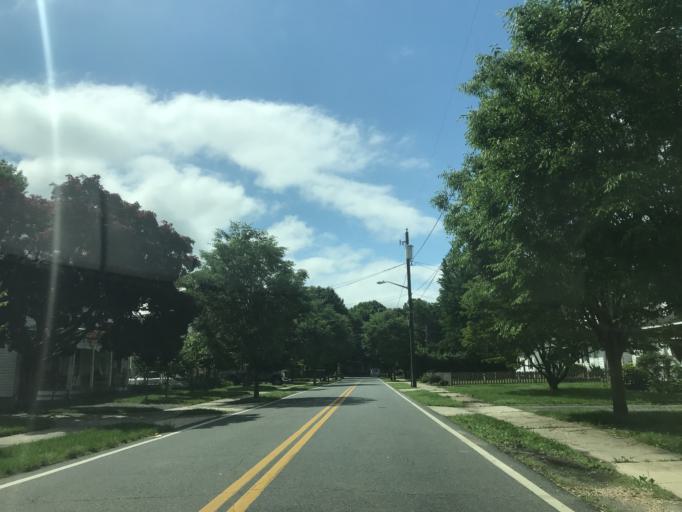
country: US
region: Maryland
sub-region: Caroline County
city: Ridgely
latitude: 38.9189
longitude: -75.9540
